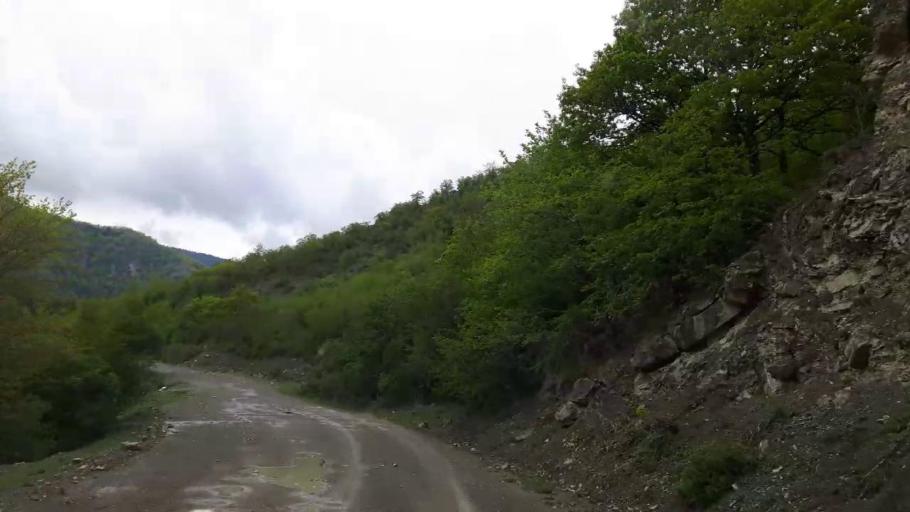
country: GE
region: Shida Kartli
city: Gori
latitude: 41.8717
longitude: 43.9859
